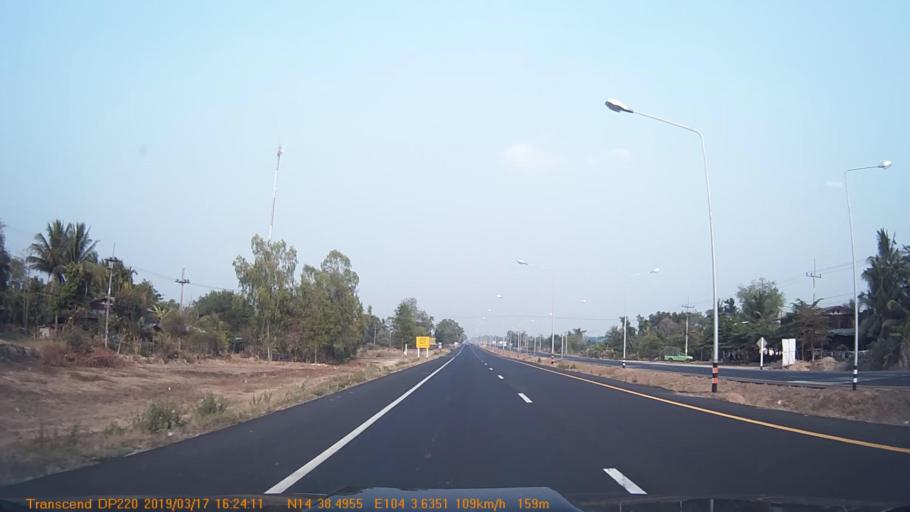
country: TH
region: Sisaket
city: Phu Sing
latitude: 14.6416
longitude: 104.0611
